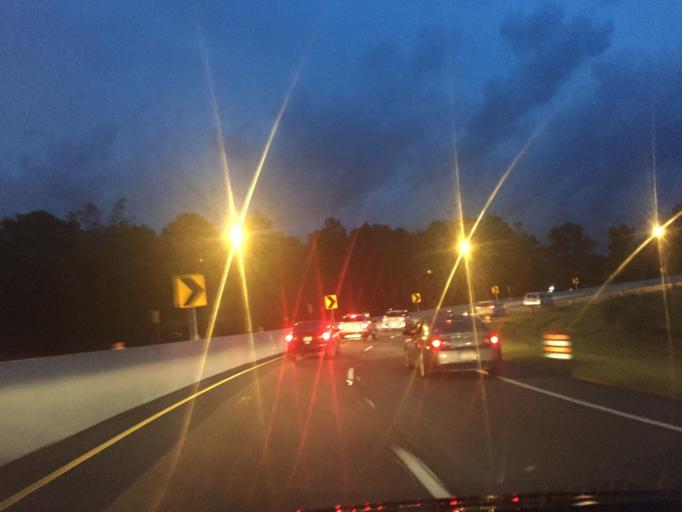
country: US
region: Georgia
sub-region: Chatham County
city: Georgetown
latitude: 31.9884
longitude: -81.2186
